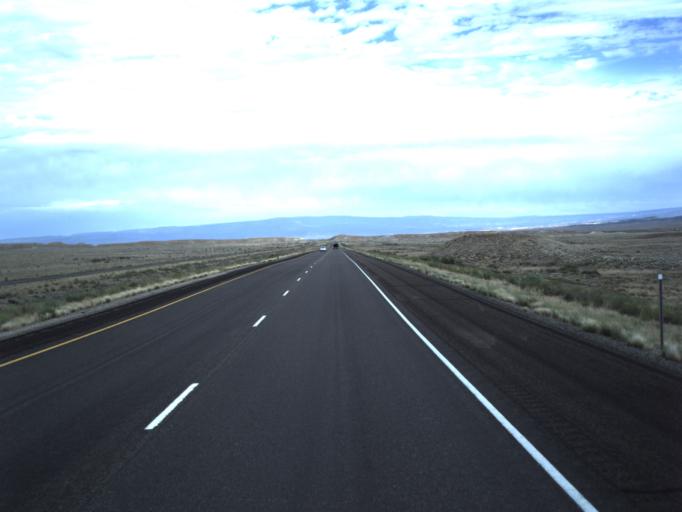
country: US
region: Utah
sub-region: Grand County
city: Moab
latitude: 38.9481
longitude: -109.6680
